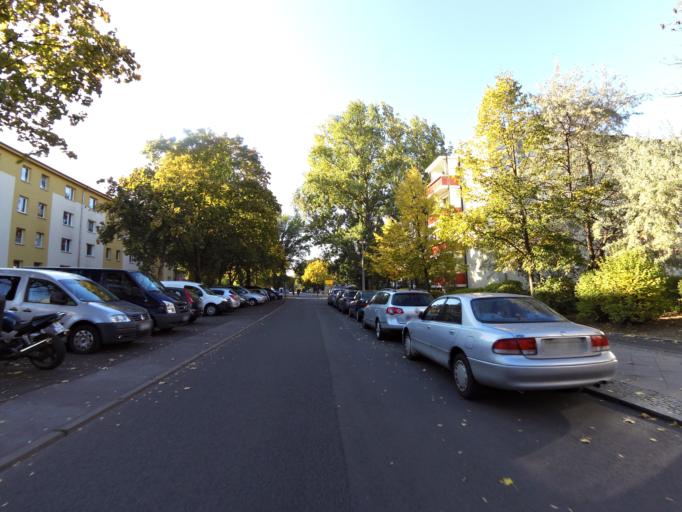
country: DE
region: Berlin
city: Oberschoneweide
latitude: 52.4624
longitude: 13.5265
